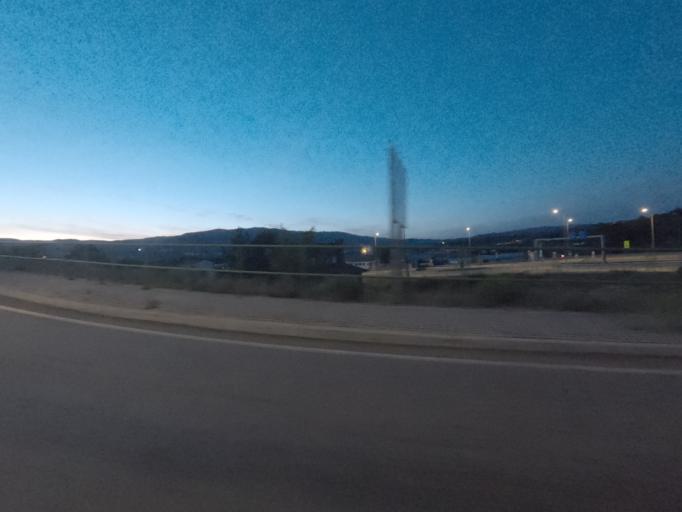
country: PT
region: Vila Real
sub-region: Vila Real
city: Vila Real
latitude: 41.2810
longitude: -7.7210
